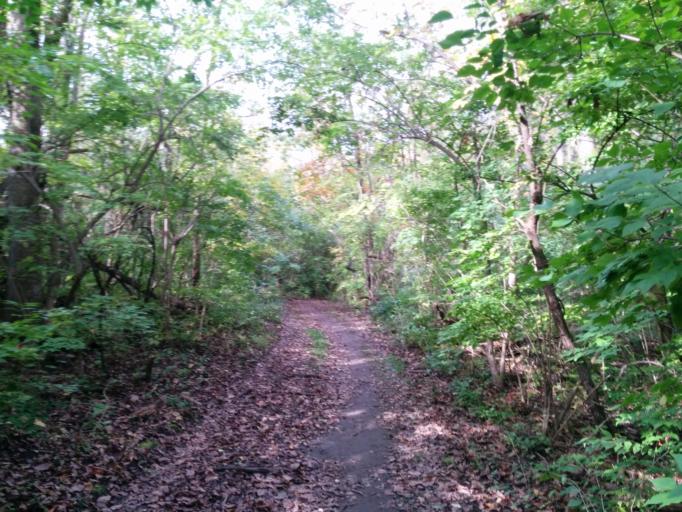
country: US
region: Illinois
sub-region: DuPage County
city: Burr Ridge
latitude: 41.7021
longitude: -87.9060
